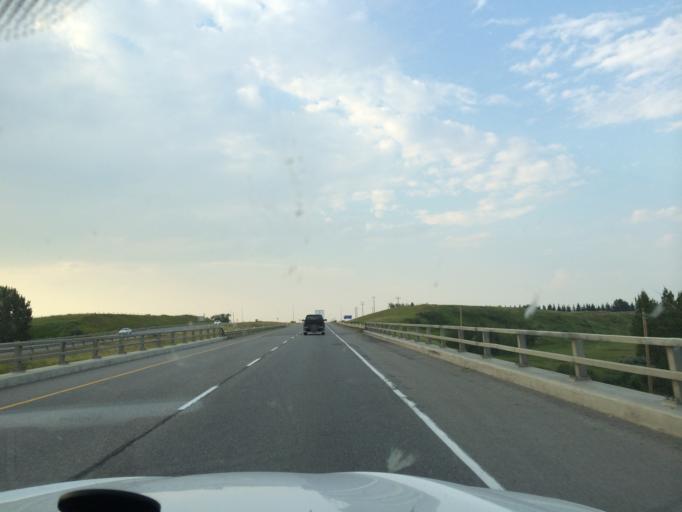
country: CA
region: Alberta
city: Okotoks
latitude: 50.7128
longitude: -113.8819
